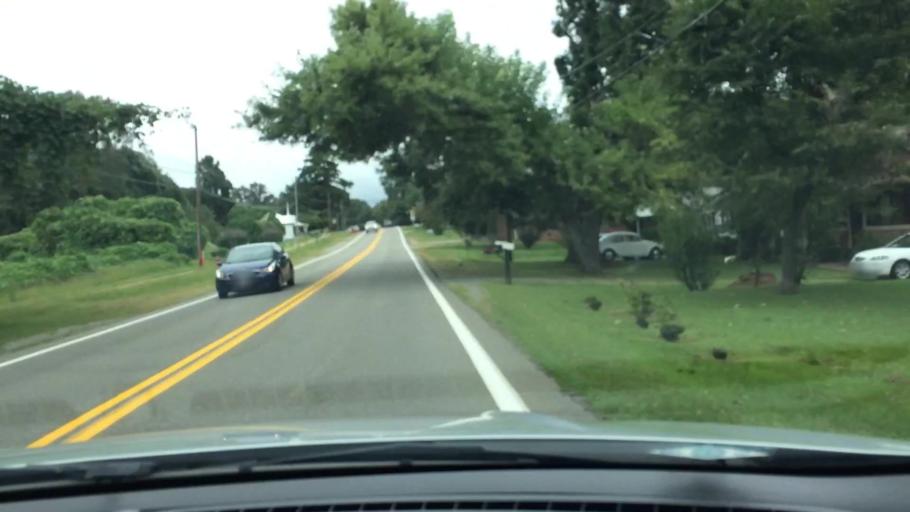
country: US
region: Virginia
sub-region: Pittsylvania County
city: Chatham
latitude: 36.8396
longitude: -79.3935
